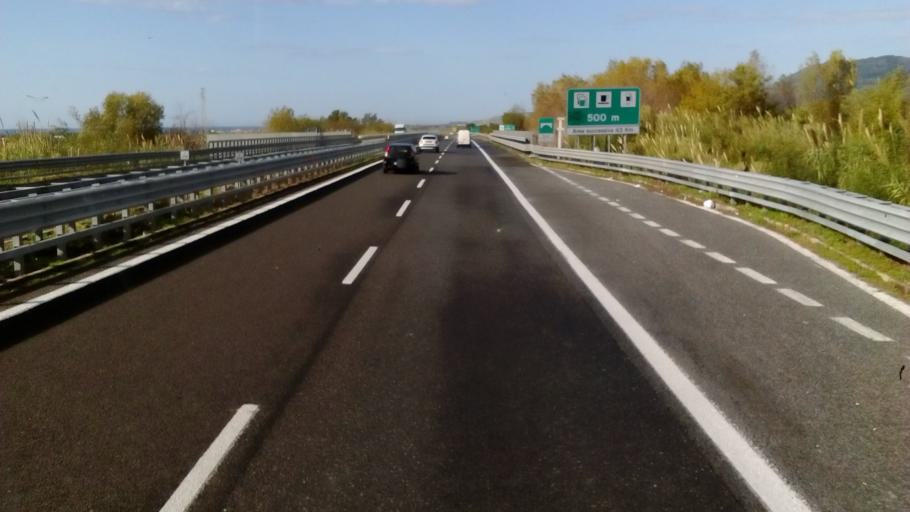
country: IT
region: Calabria
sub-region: Provincia di Catanzaro
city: Santa Eufemia Lamezia
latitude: 38.9277
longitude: 16.2449
